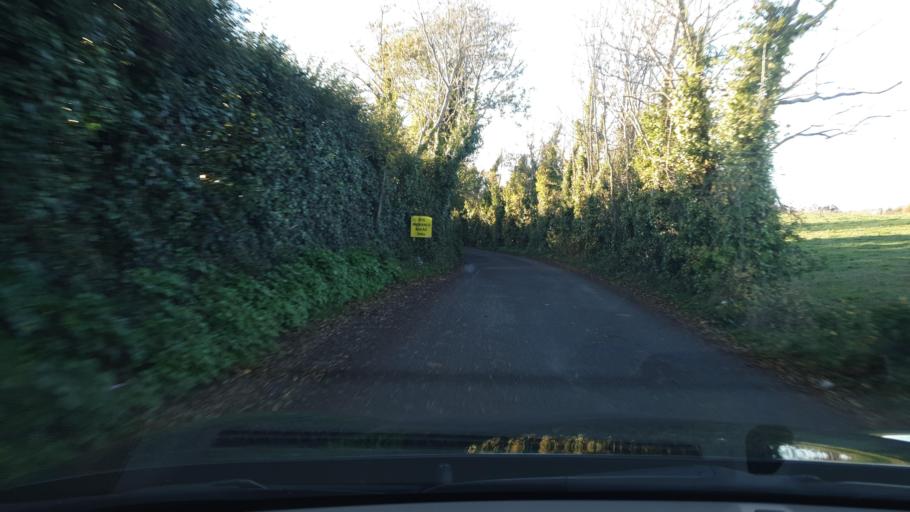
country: IE
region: Leinster
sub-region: An Mhi
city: Stamullin
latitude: 53.6552
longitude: -6.3019
